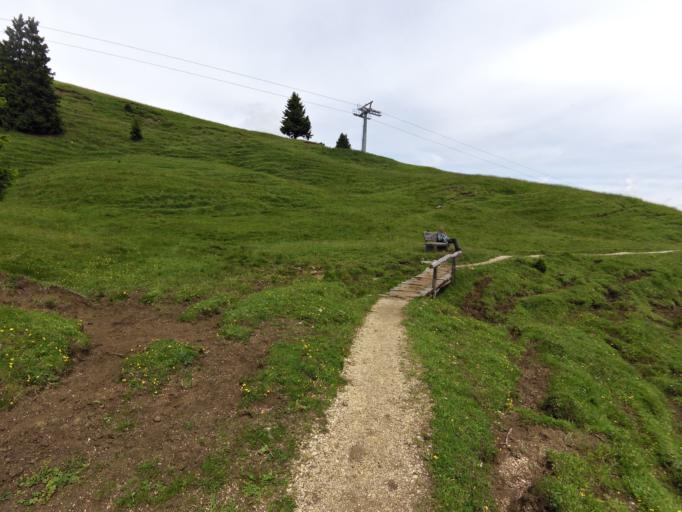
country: IT
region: Trentino-Alto Adige
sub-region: Bolzano
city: Ortisei
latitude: 46.5229
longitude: 11.6510
